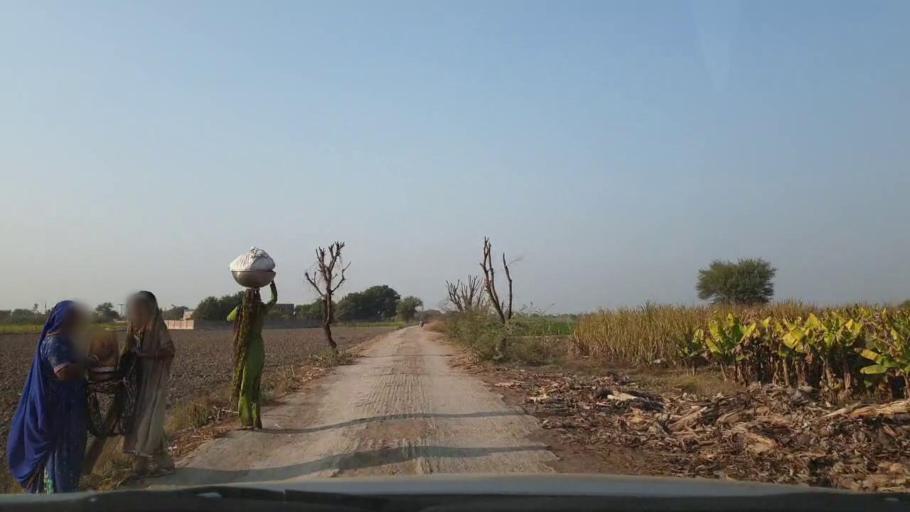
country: PK
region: Sindh
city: Tando Adam
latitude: 25.6792
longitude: 68.6346
